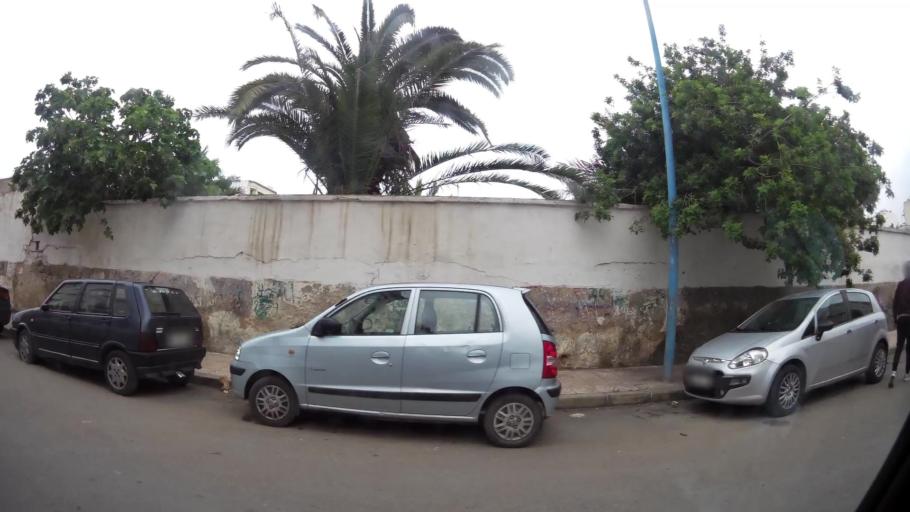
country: MA
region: Grand Casablanca
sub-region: Casablanca
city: Casablanca
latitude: 33.6021
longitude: -7.6341
